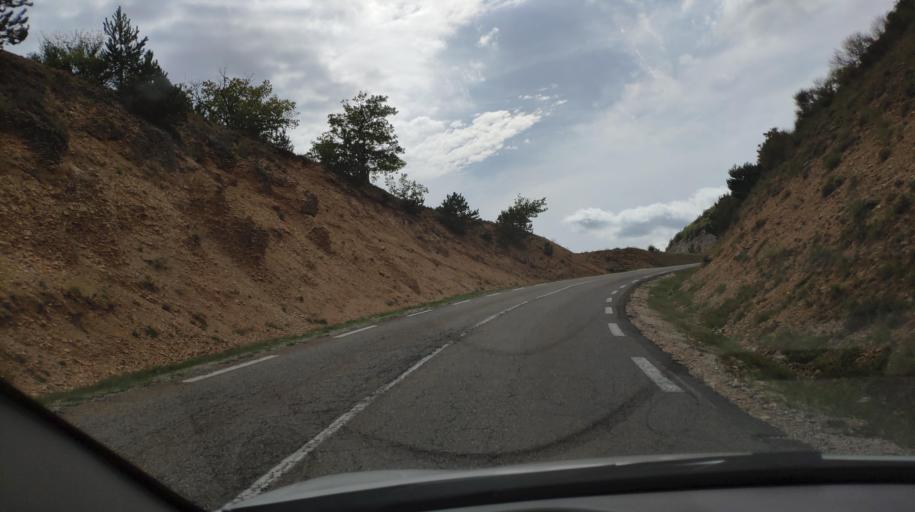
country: FR
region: Provence-Alpes-Cote d'Azur
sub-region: Departement du Vaucluse
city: Sault
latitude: 44.0896
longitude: 5.3688
